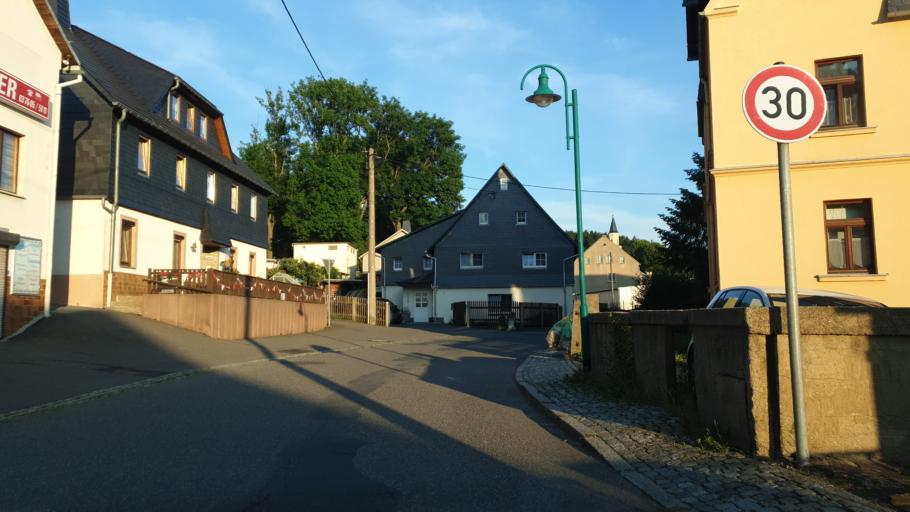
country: DE
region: Saxony
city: Lossnitz
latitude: 50.6649
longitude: 12.7221
